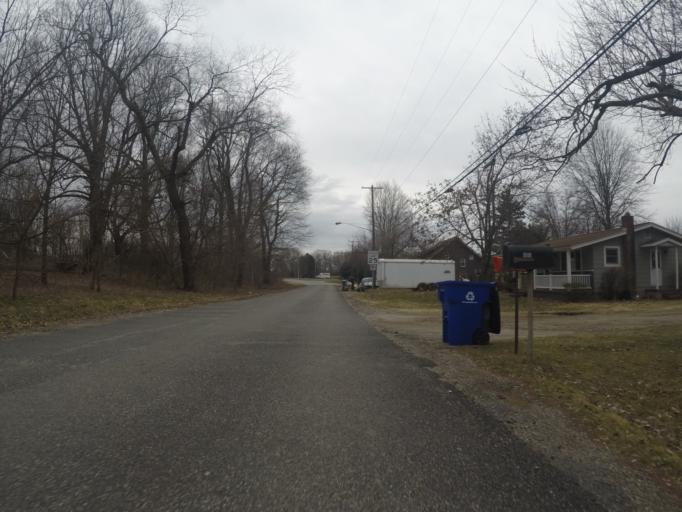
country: US
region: Ohio
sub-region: Portage County
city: Kent
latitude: 41.1585
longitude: -81.3101
